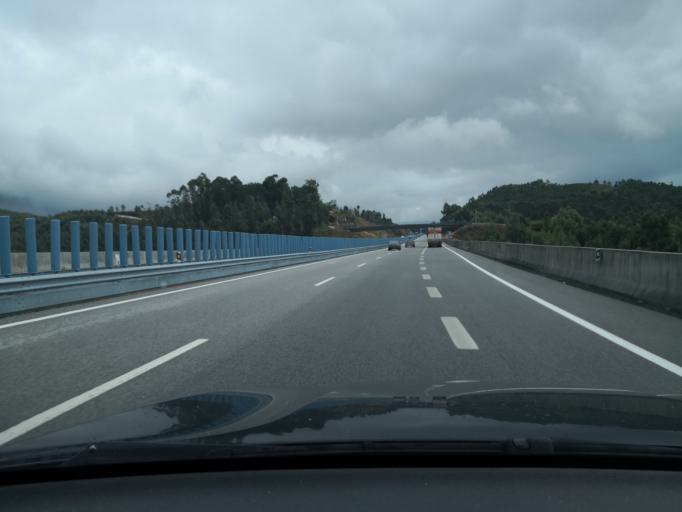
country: PT
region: Porto
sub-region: Lousada
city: Lousada
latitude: 41.2958
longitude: -8.2995
